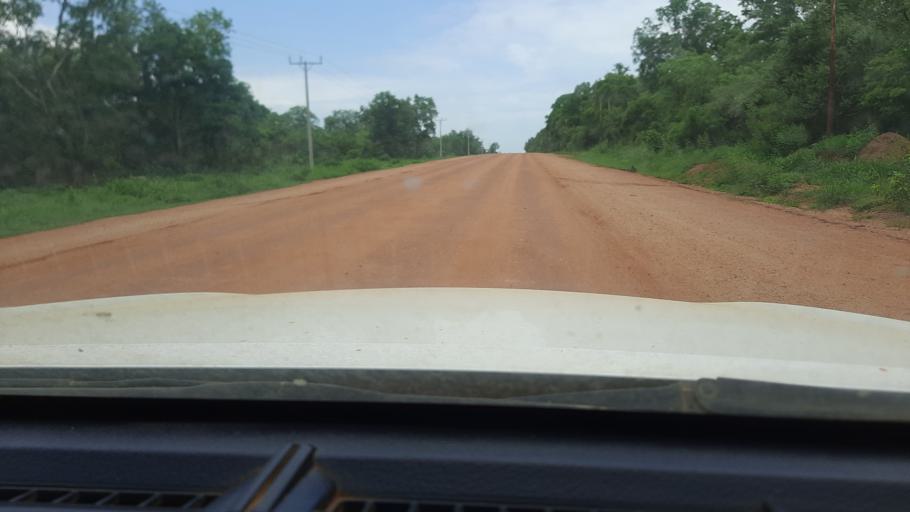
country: ET
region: Gambela
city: Gambela
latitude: 8.1354
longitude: 34.5786
